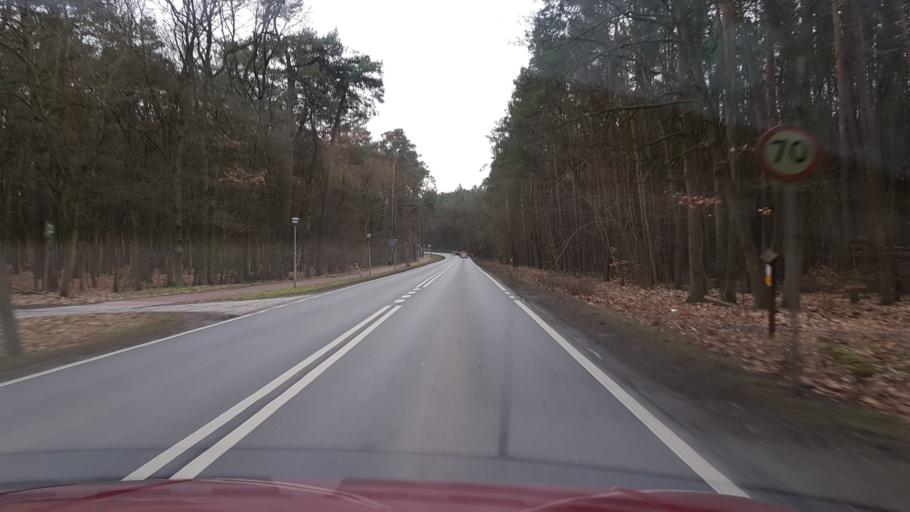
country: PL
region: West Pomeranian Voivodeship
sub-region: Szczecin
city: Szczecin
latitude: 53.4854
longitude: 14.4836
